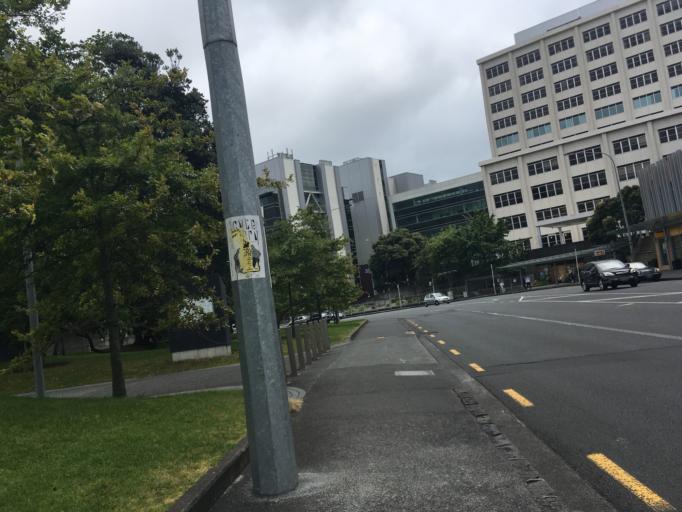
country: NZ
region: Auckland
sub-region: Auckland
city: Auckland
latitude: -36.8619
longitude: 174.7703
